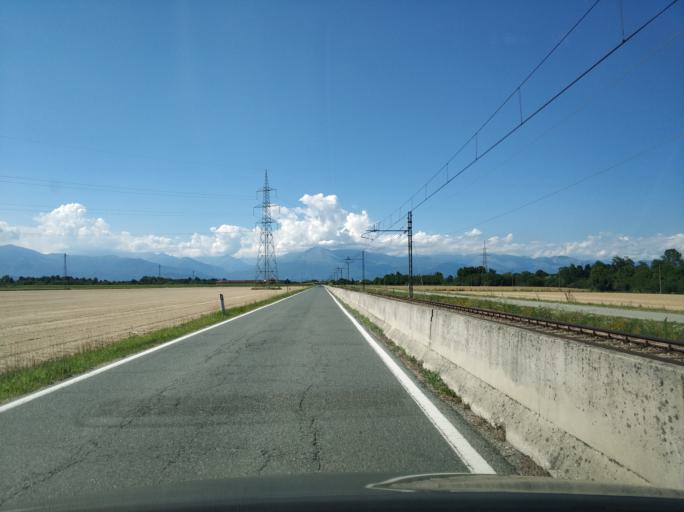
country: IT
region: Piedmont
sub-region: Provincia di Torino
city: San Benigno Canavese
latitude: 45.2428
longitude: 7.7726
